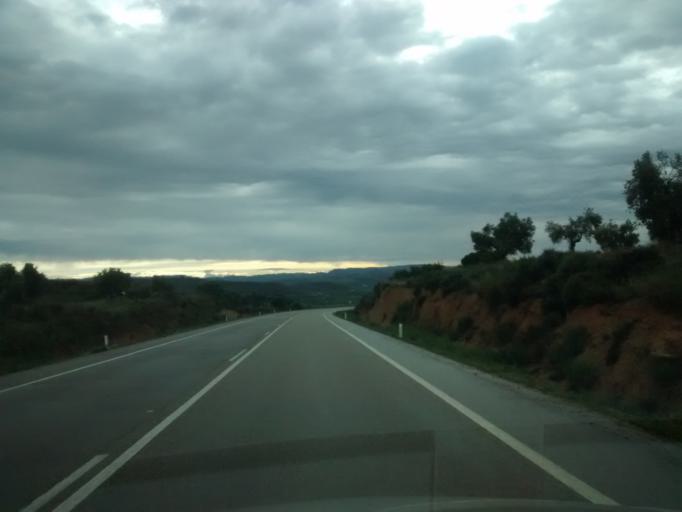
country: ES
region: Aragon
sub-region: Provincia de Zaragoza
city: Maella
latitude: 41.1123
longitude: 0.1600
